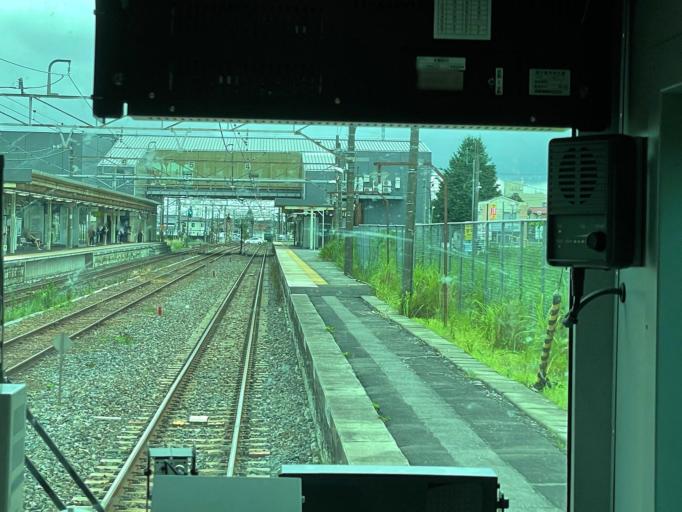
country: JP
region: Tochigi
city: Ujiie
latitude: 36.6322
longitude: 139.9793
